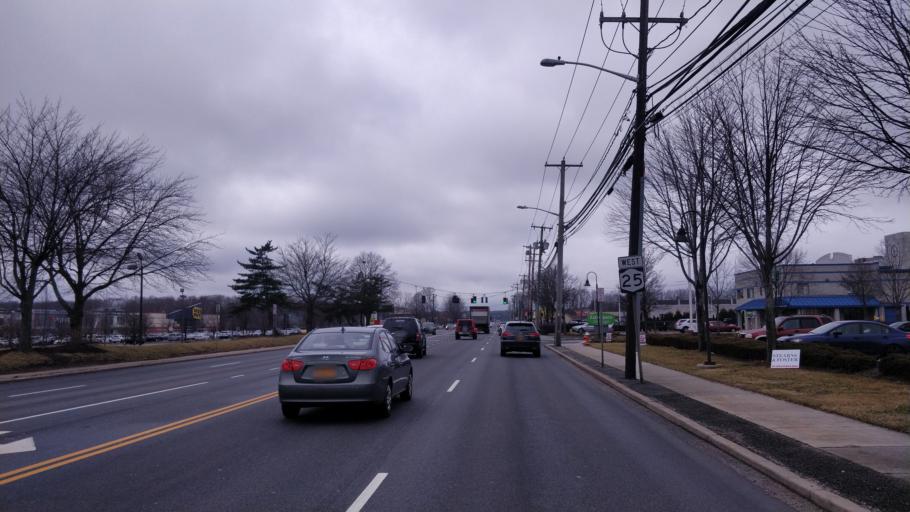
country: US
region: New York
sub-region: Suffolk County
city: Elwood
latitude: 40.8402
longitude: -73.3159
